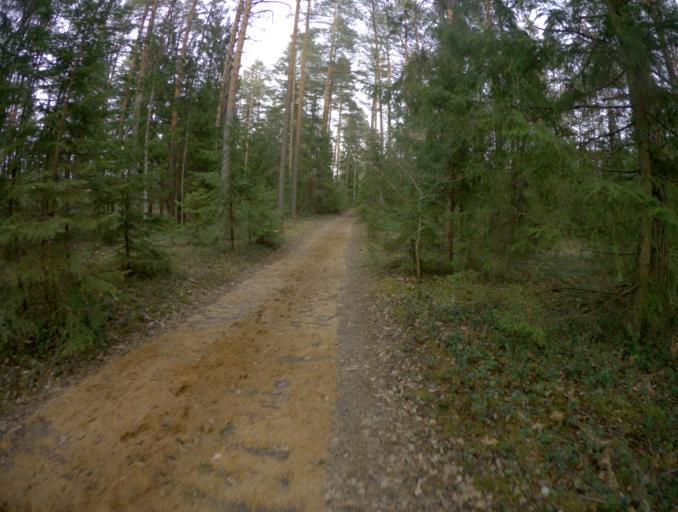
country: RU
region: Vladimir
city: Kommunar
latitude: 56.0754
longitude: 40.5164
